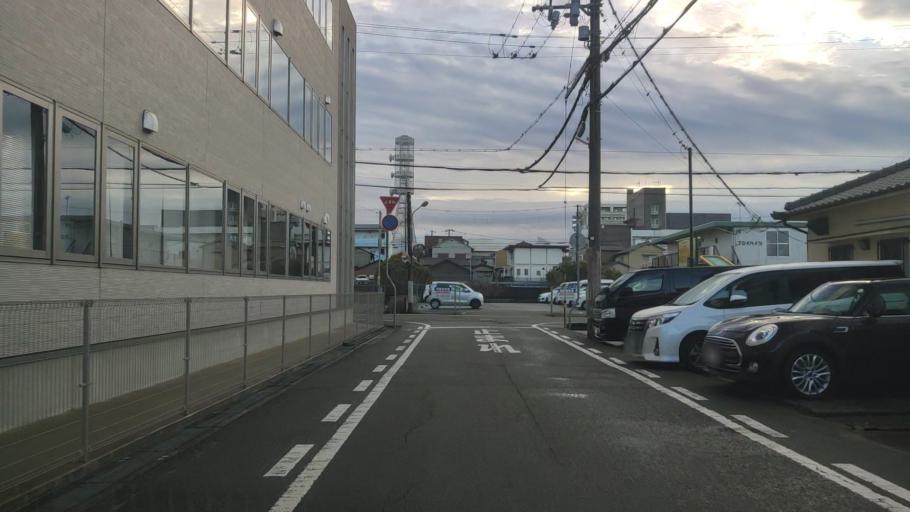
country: JP
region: Hyogo
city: Himeji
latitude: 34.8236
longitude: 134.6910
